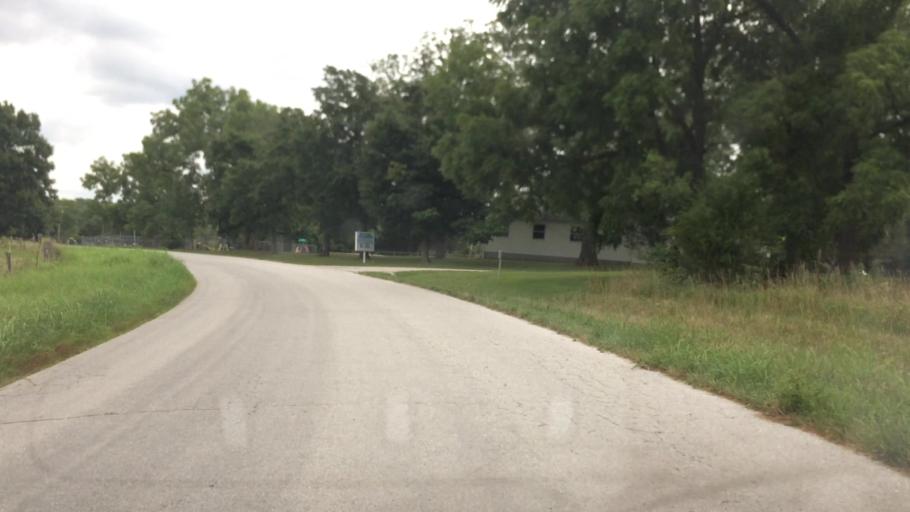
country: US
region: Missouri
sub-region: Greene County
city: Strafford
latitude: 37.3207
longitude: -93.0588
